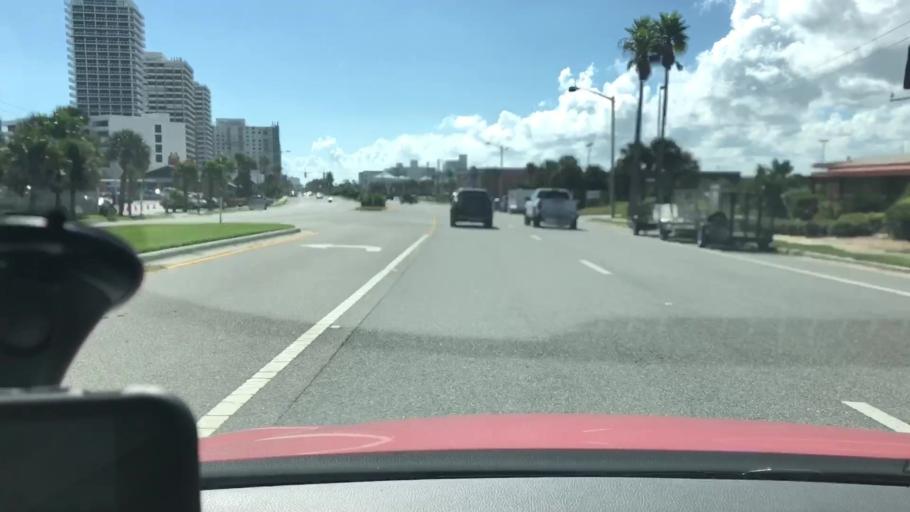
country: US
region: Florida
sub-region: Volusia County
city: Holly Hill
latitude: 29.2709
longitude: -81.0298
